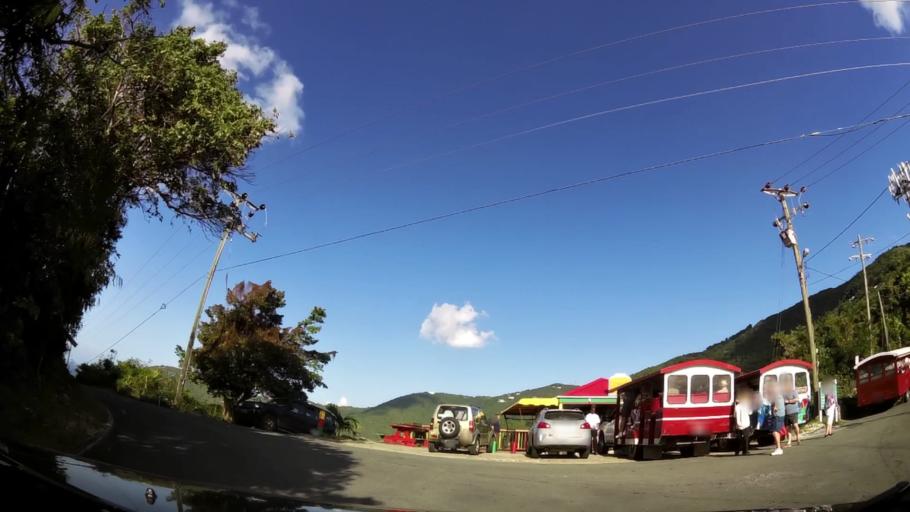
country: VG
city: Road Town
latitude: 18.4162
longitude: -64.6682
